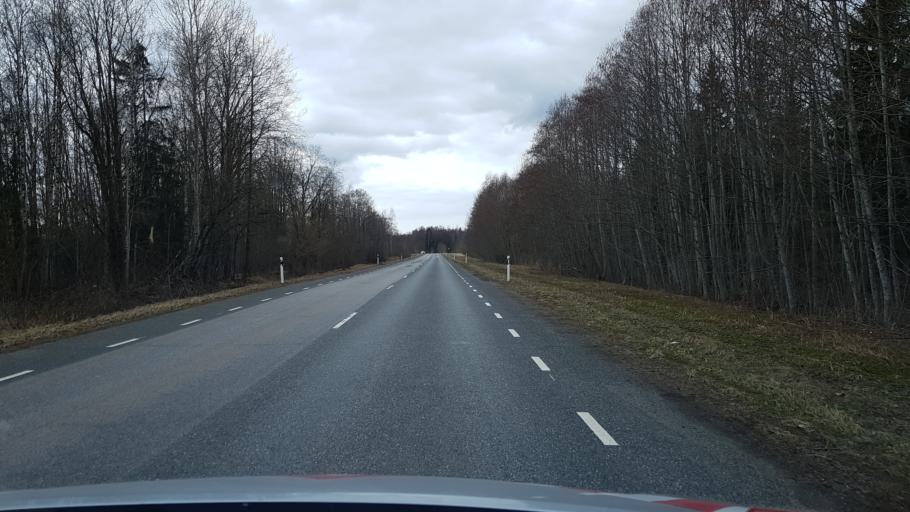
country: EE
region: Ida-Virumaa
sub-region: Narva-Joesuu linn
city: Narva-Joesuu
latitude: 59.3513
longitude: 28.0500
